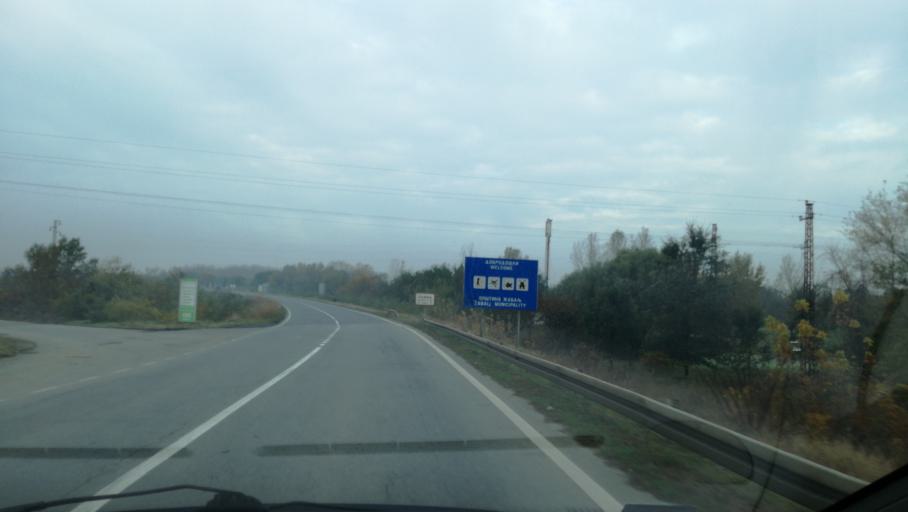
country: RS
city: Taras
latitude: 45.3993
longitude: 20.2085
